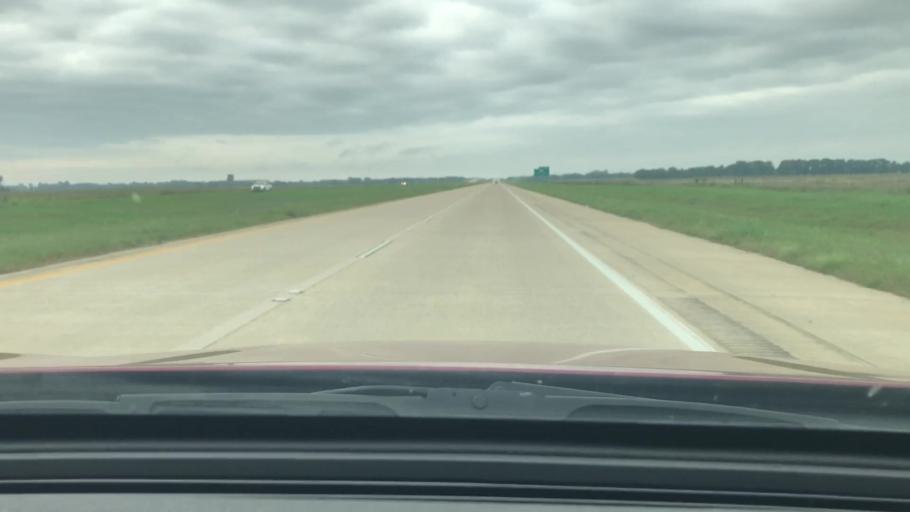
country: US
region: Louisiana
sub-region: Caddo Parish
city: Oil City
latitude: 32.7157
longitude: -93.8676
